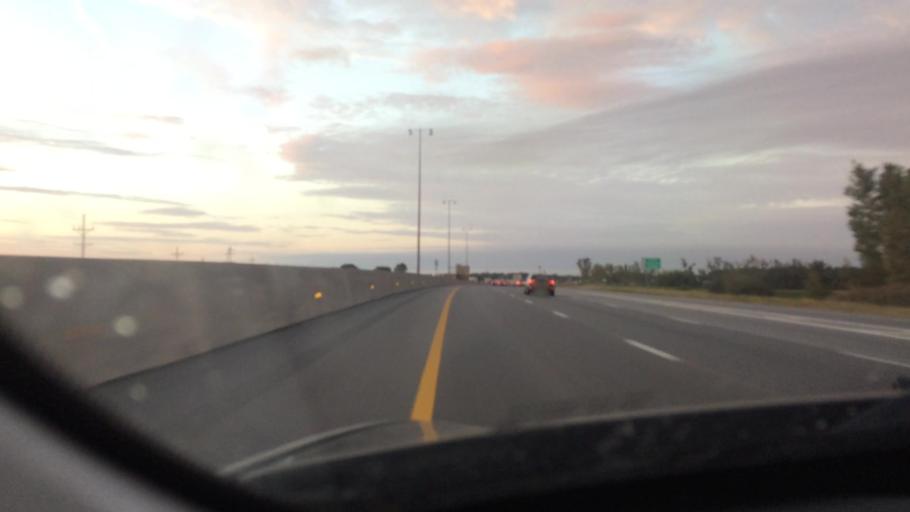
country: US
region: Ohio
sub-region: Wood County
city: North Baltimore
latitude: 41.1686
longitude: -83.6499
